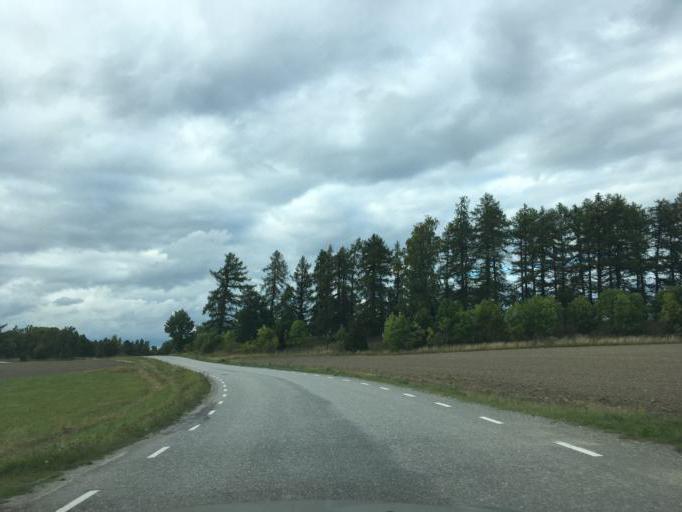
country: SE
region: Vaestmanland
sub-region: Vasteras
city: Tillberga
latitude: 59.5759
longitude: 16.7288
